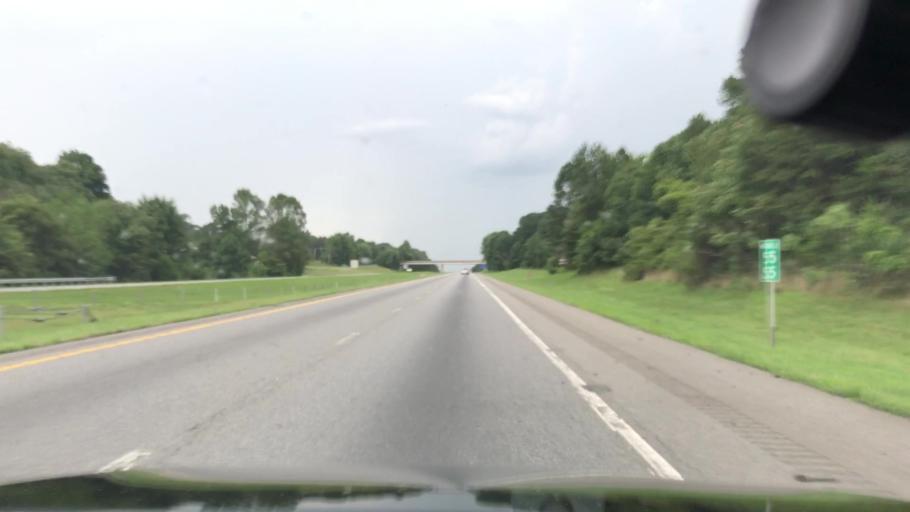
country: US
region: North Carolina
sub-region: Iredell County
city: Statesville
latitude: 35.8641
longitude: -80.8644
